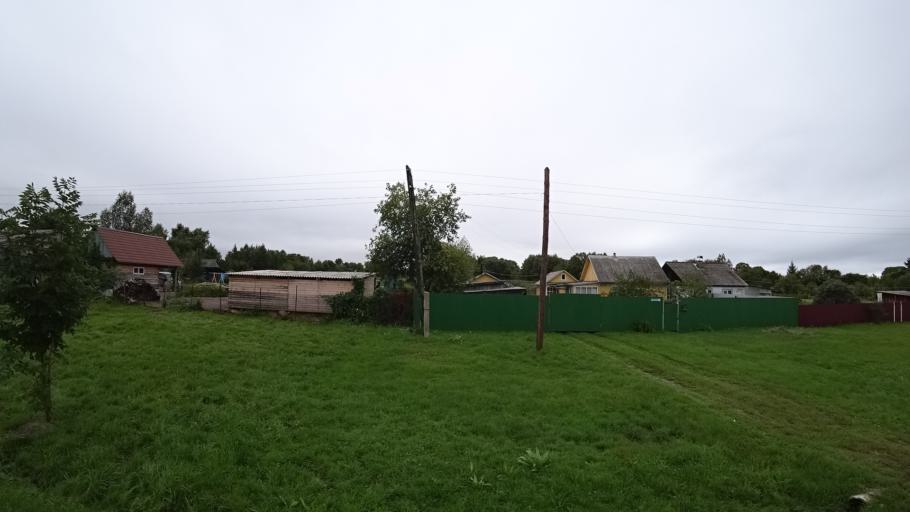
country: RU
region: Primorskiy
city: Monastyrishche
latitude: 44.0906
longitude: 132.5772
